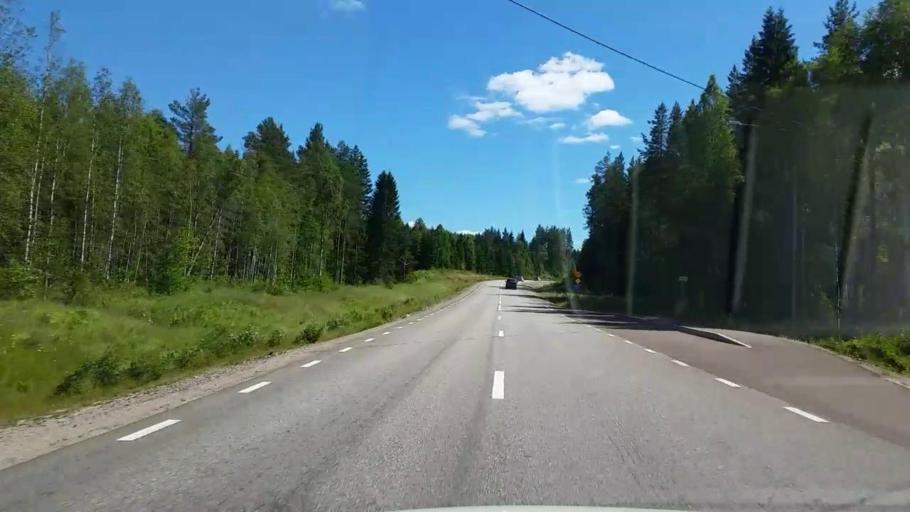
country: SE
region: Gaevleborg
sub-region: Ovanakers Kommun
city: Edsbyn
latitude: 61.1776
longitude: 15.8811
